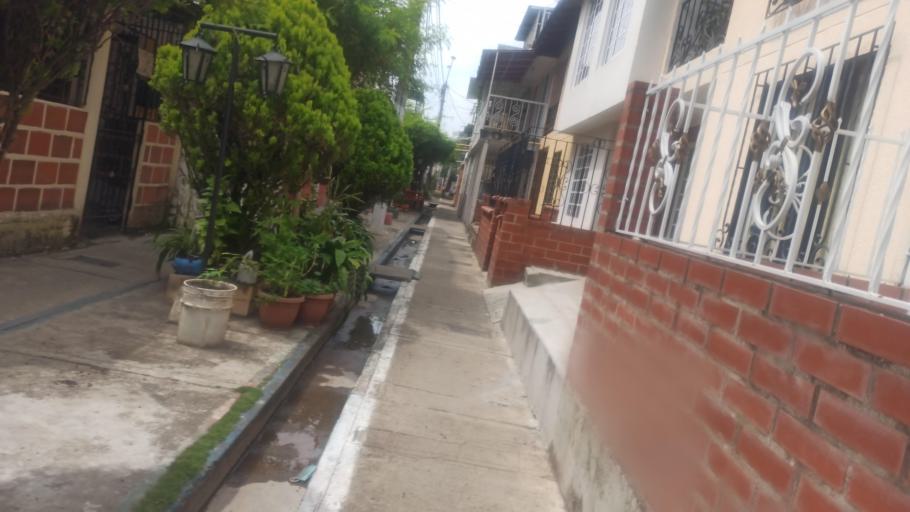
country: CO
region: Valle del Cauca
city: Jamundi
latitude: 3.2347
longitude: -76.5100
